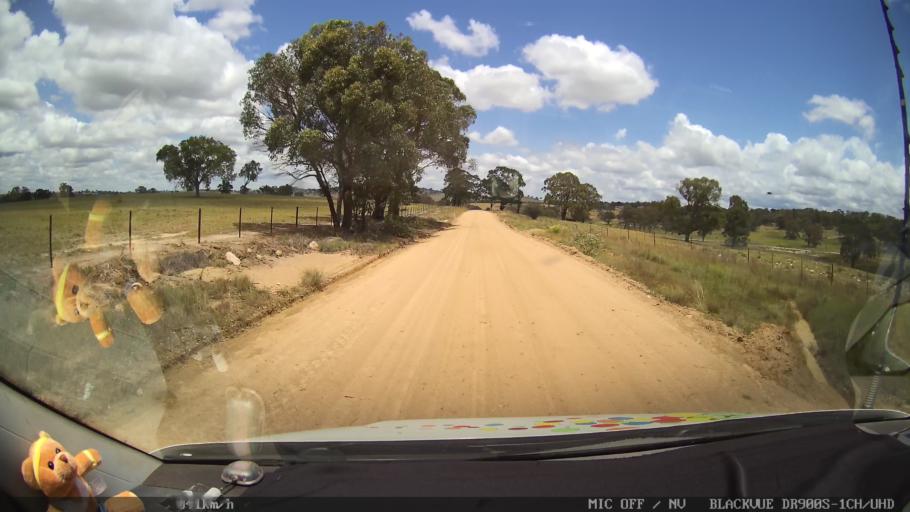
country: AU
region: New South Wales
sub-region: Glen Innes Severn
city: Glen Innes
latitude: -29.3490
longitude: 151.8869
